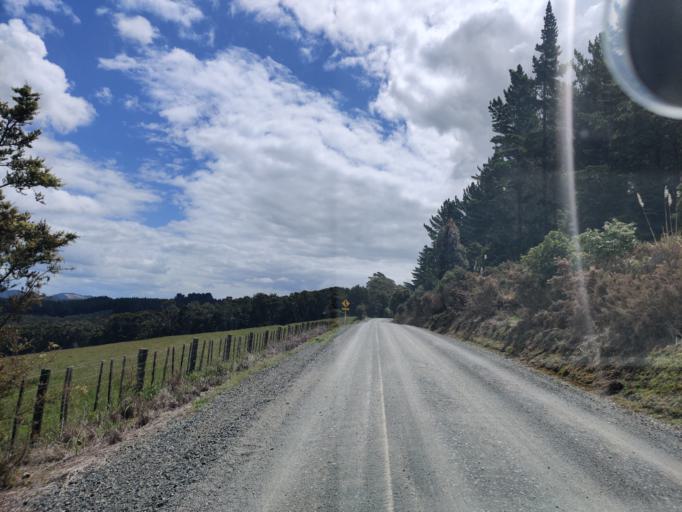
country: NZ
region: Northland
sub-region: Far North District
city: Paihia
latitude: -35.2594
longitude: 174.0634
